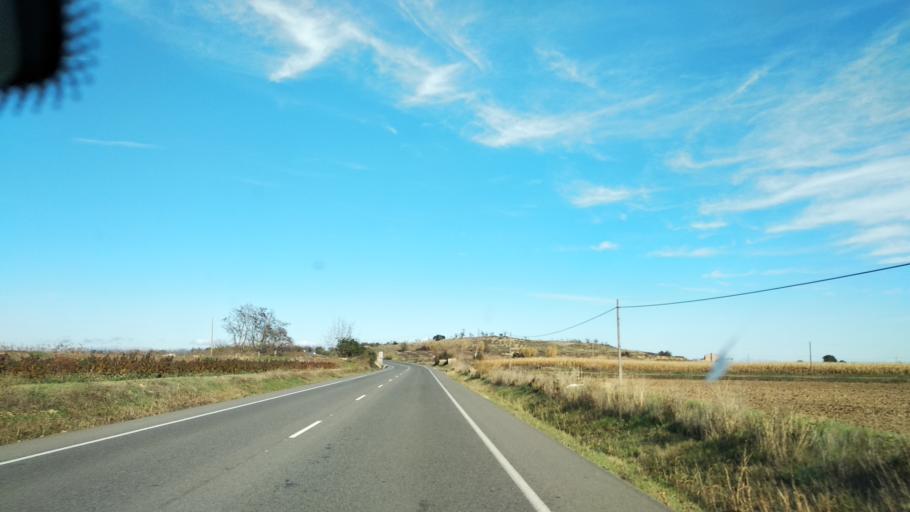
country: ES
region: Catalonia
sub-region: Provincia de Lleida
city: Alcoletge
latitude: 41.6663
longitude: 0.6661
